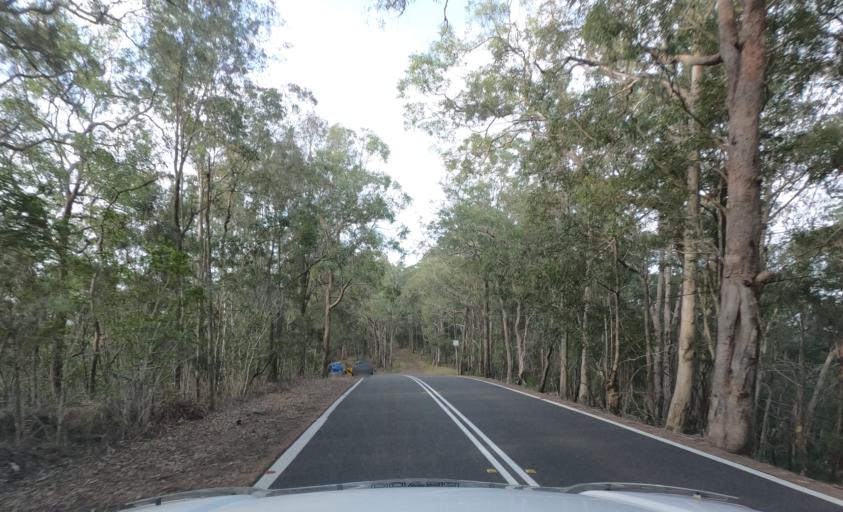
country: AU
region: New South Wales
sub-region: Wyong Shire
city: Little Jilliby
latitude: -33.2302
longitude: 151.2717
